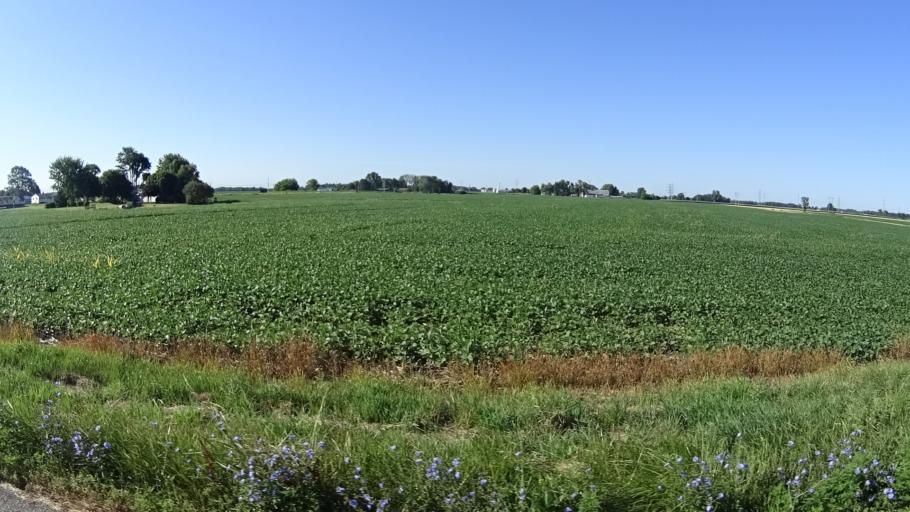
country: US
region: Ohio
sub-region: Erie County
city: Sandusky
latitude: 41.3971
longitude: -82.7349
